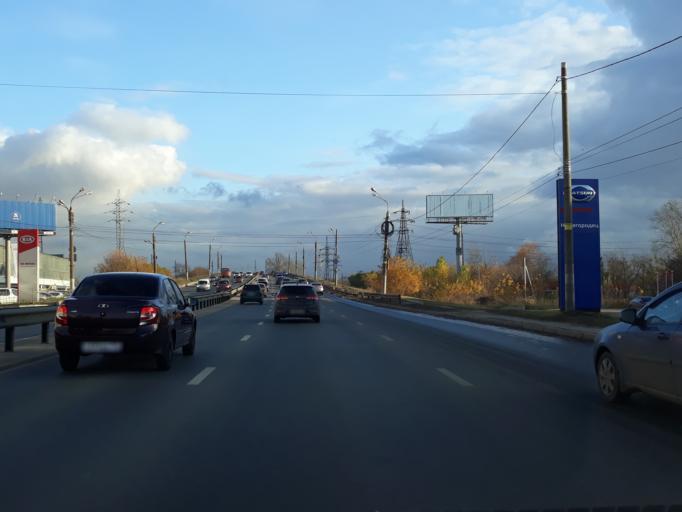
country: RU
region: Nizjnij Novgorod
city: Nizhniy Novgorod
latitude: 56.3095
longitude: 43.9005
